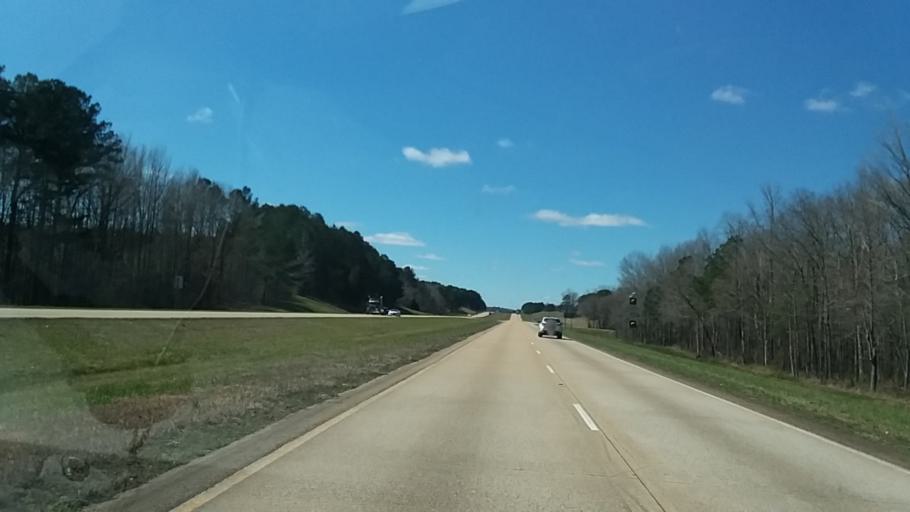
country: US
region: Mississippi
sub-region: Tishomingo County
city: Iuka
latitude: 34.8058
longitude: -88.2527
